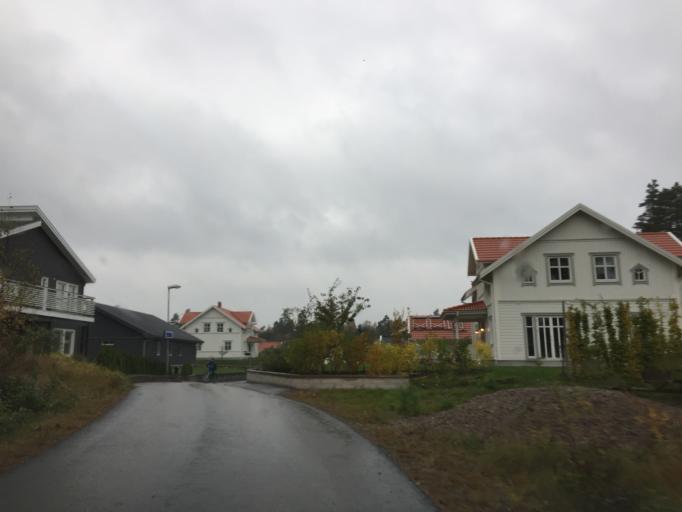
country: SE
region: Vaestra Goetaland
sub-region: Trollhattan
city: Trollhattan
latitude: 58.3212
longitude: 12.2924
